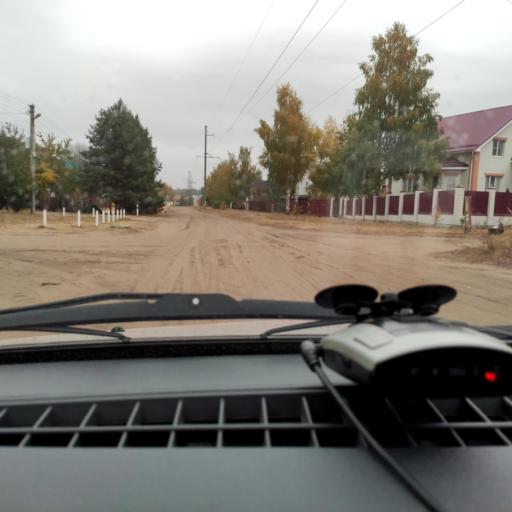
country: RU
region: Voronezj
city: Podgornoye
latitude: 51.7614
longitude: 39.1772
